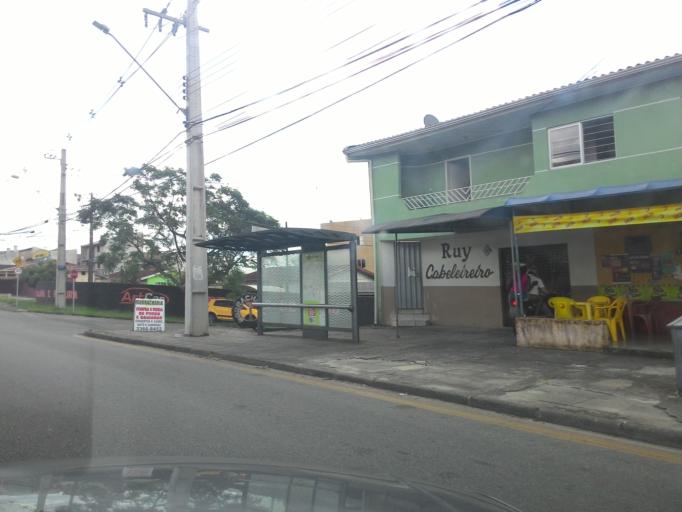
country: BR
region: Parana
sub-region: Pinhais
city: Pinhais
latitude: -25.4520
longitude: -49.2233
